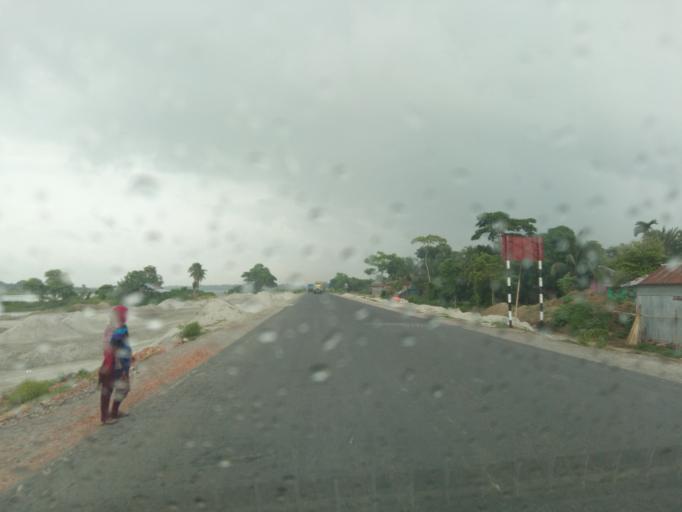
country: BD
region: Dhaka
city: Char Bhadrasan
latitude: 23.3694
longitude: 90.0738
